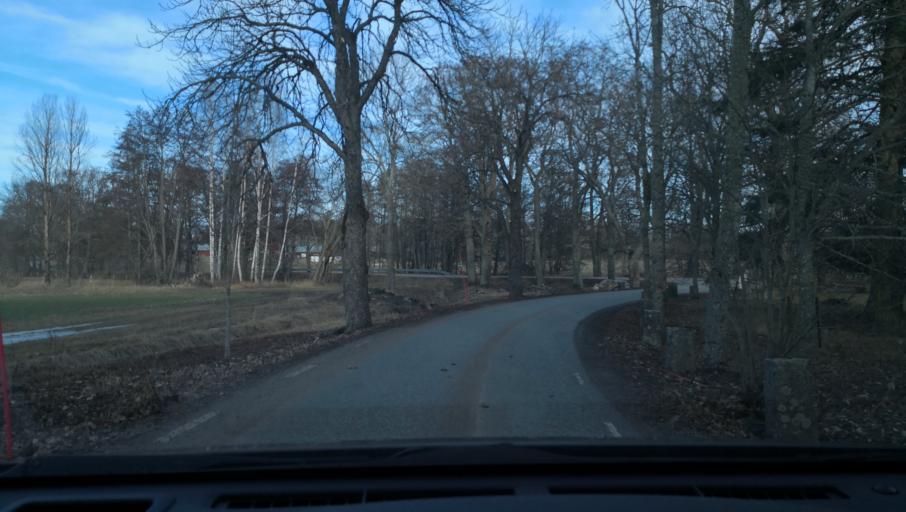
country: SE
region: Uppsala
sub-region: Enkopings Kommun
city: Grillby
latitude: 59.5419
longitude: 17.2007
